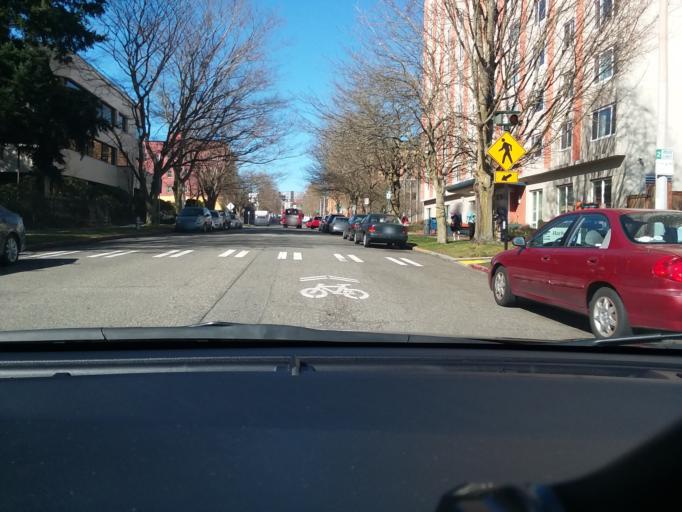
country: US
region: Washington
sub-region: Pierce County
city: Tacoma
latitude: 47.2536
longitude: -122.4431
